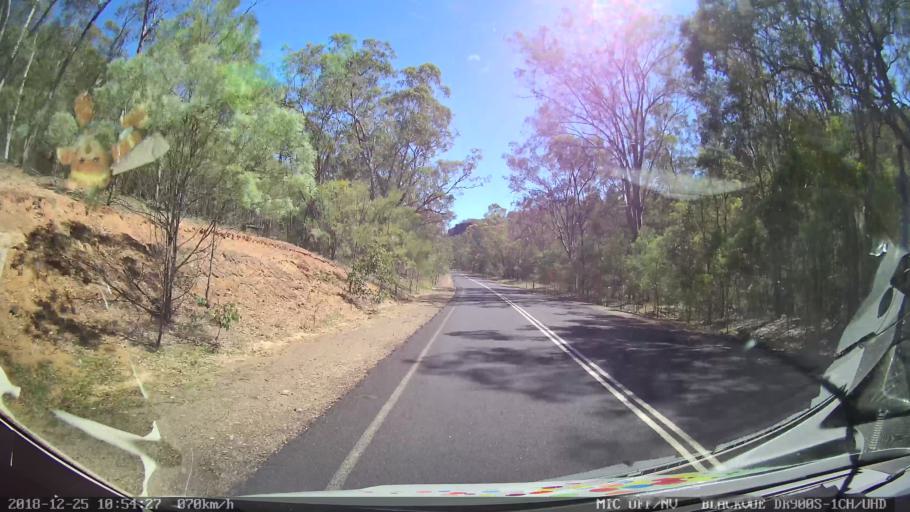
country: AU
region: New South Wales
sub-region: Upper Hunter Shire
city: Merriwa
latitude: -32.4097
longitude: 150.2731
